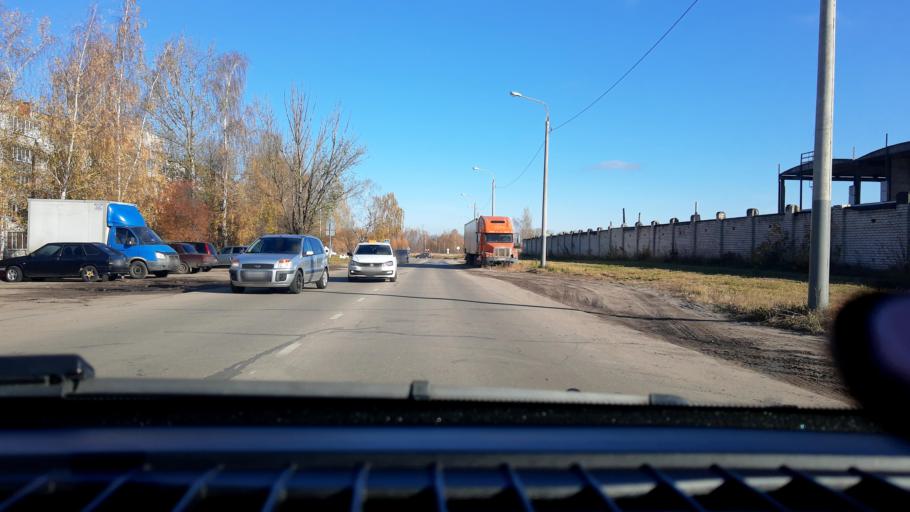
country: RU
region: Nizjnij Novgorod
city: Kstovo
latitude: 56.1492
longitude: 44.2197
